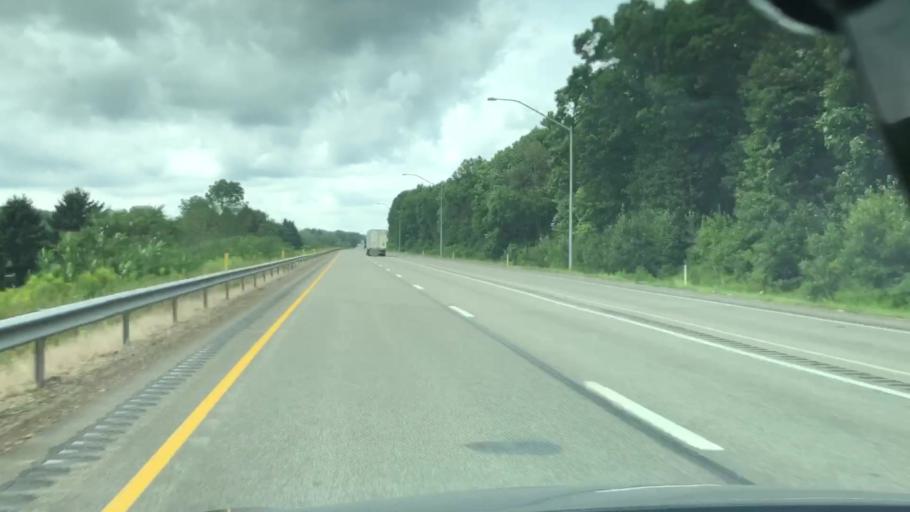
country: US
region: Pennsylvania
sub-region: Crawford County
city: Meadville
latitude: 41.6256
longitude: -80.1842
